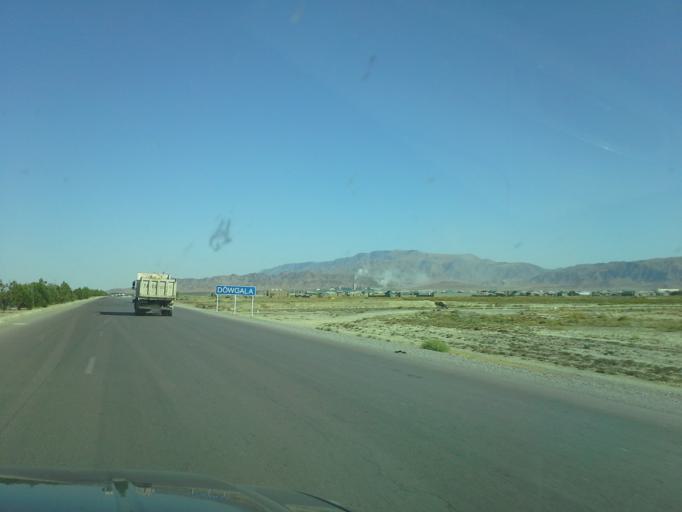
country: TM
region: Ahal
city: Baharly
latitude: 38.3087
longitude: 57.6170
